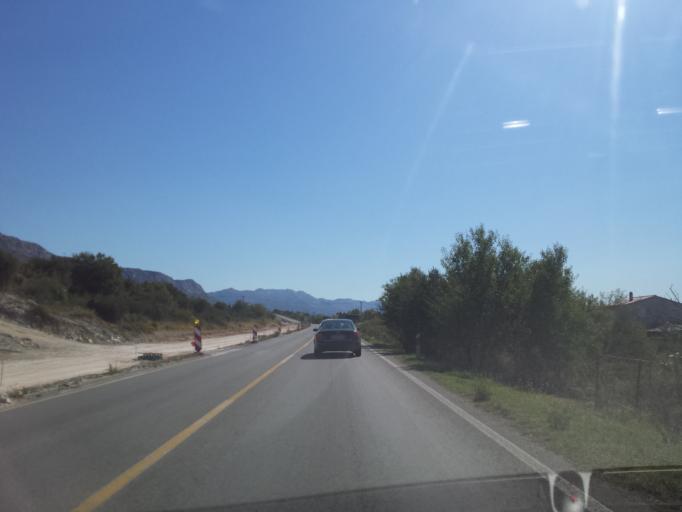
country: HR
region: Splitsko-Dalmatinska
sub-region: Grad Split
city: Split
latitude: 43.5578
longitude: 16.3707
